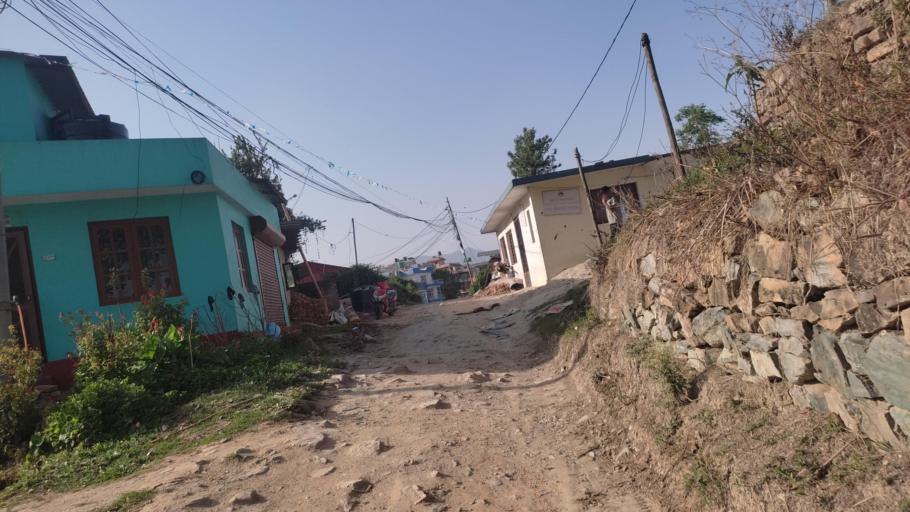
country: NP
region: Central Region
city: Kirtipur
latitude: 27.6598
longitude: 85.2790
